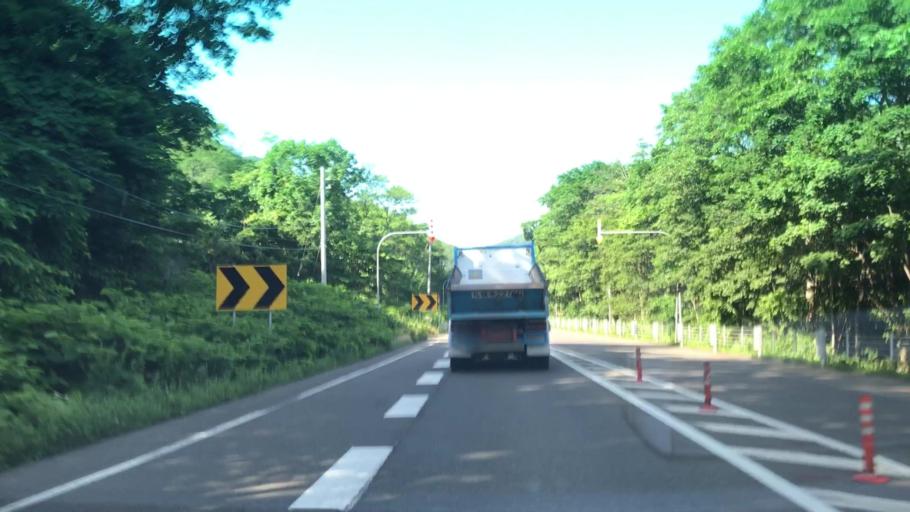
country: JP
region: Hokkaido
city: Iwanai
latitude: 43.0186
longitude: 140.6669
